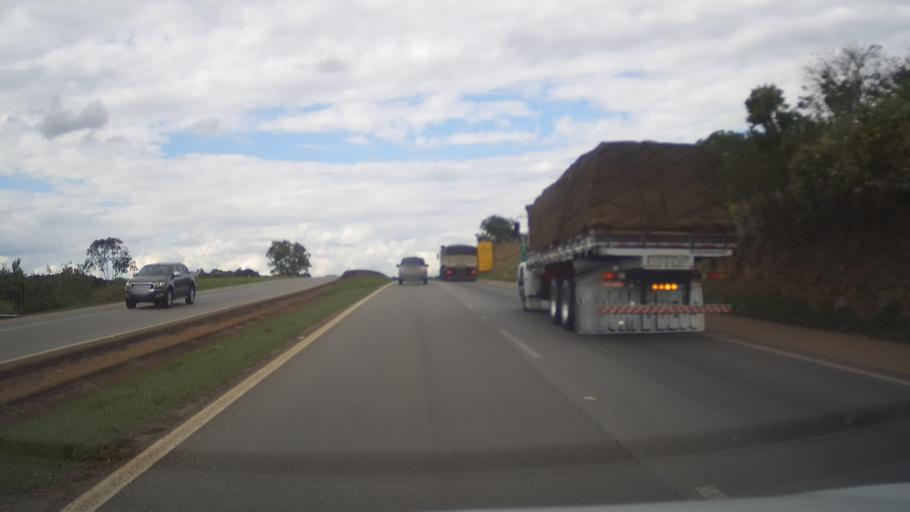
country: BR
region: Minas Gerais
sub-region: Itauna
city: Itauna
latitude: -20.3091
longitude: -44.4492
